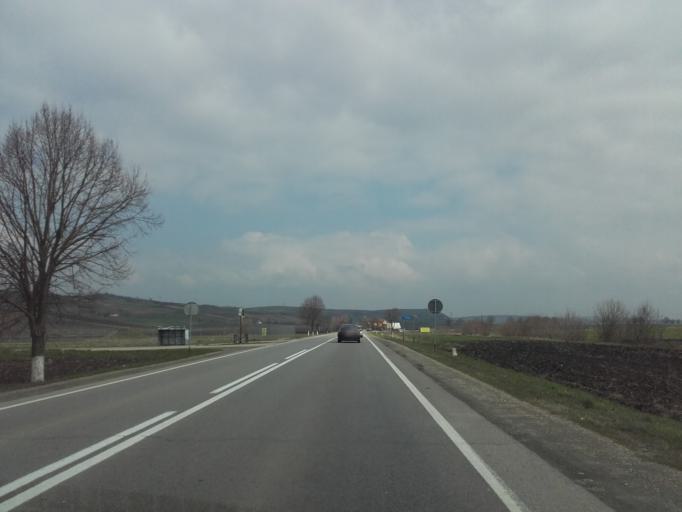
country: RO
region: Mures
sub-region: Comuna Chetani
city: Chetani
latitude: 46.4677
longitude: 24.0493
